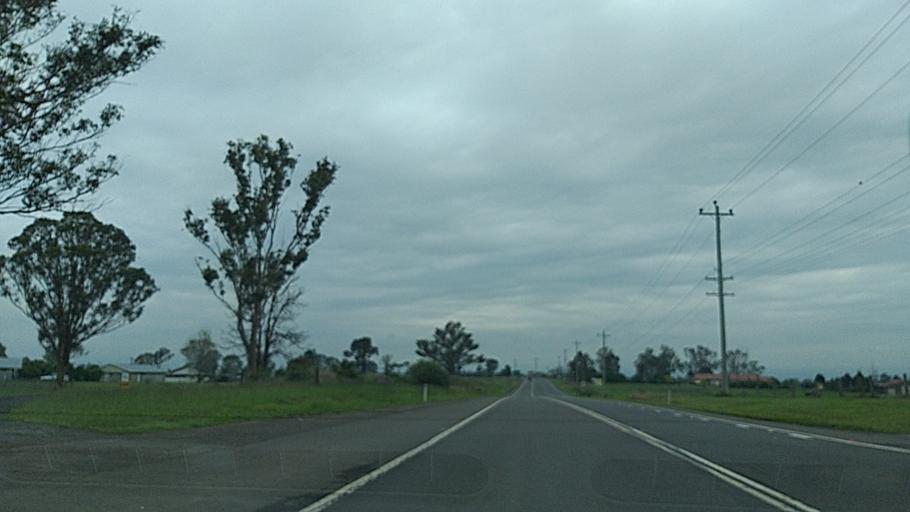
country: AU
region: New South Wales
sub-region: Liverpool
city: Luddenham
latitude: -33.8695
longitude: 150.6932
